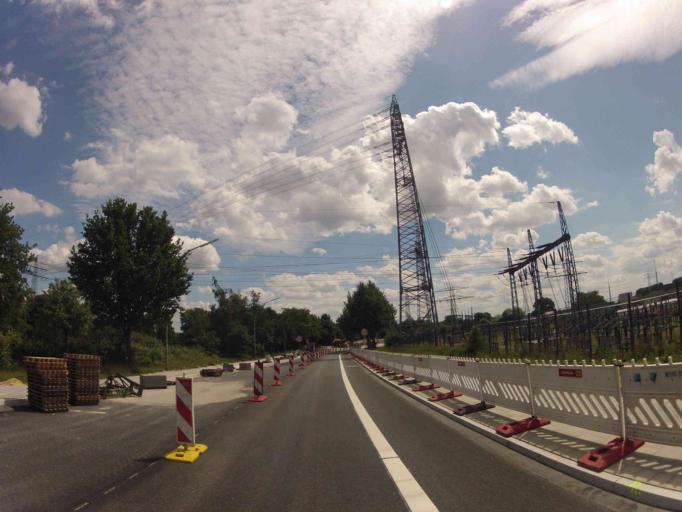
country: DE
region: Hamburg
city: Rothenburgsort
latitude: 53.5284
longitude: 10.0686
